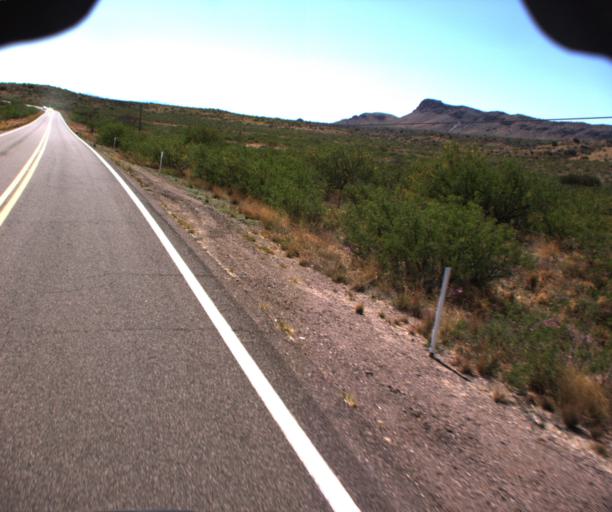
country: US
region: Arizona
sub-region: Cochise County
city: Douglas
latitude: 31.4827
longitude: -109.4120
